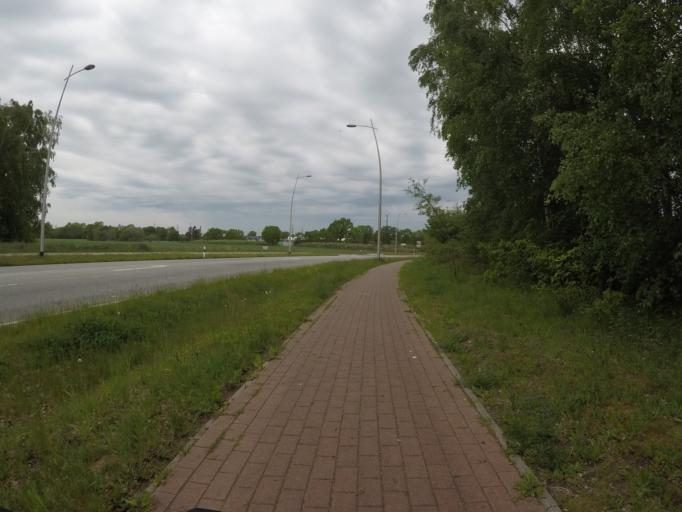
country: DE
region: Schleswig-Holstein
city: Norderstedt
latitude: 53.7304
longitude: 9.9840
